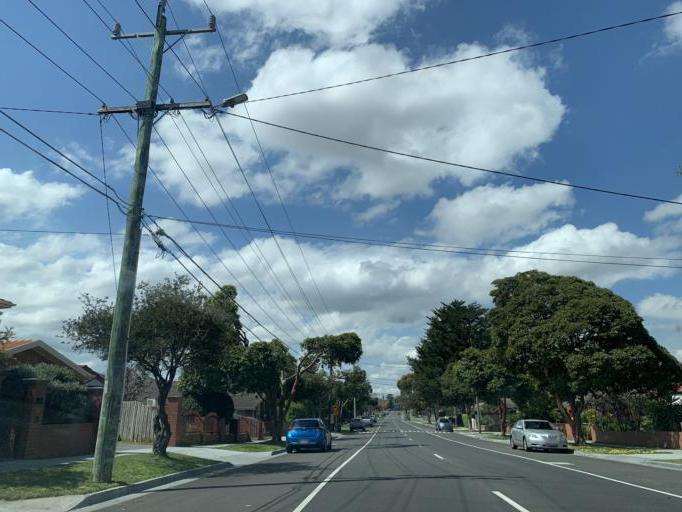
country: AU
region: Victoria
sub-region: Kingston
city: Mordialloc
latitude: -38.0018
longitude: 145.0941
